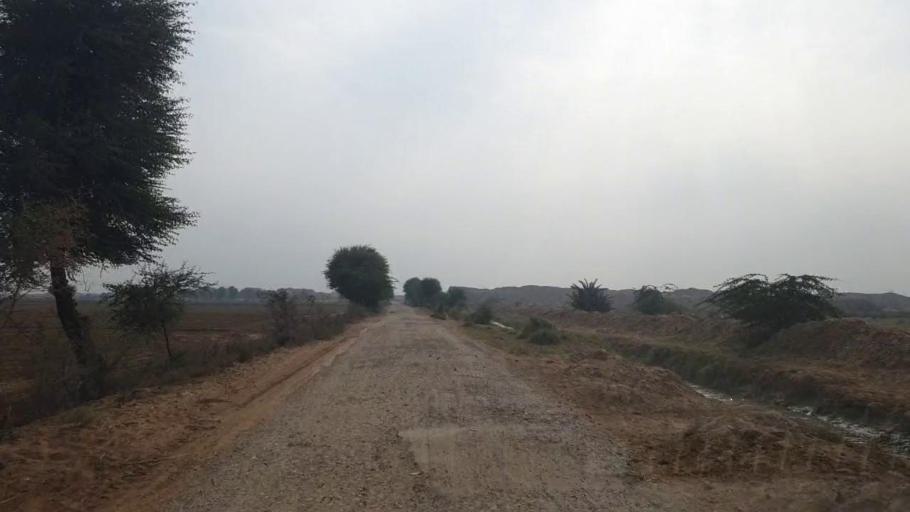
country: PK
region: Sindh
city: Sann
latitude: 26.0191
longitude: 68.1439
